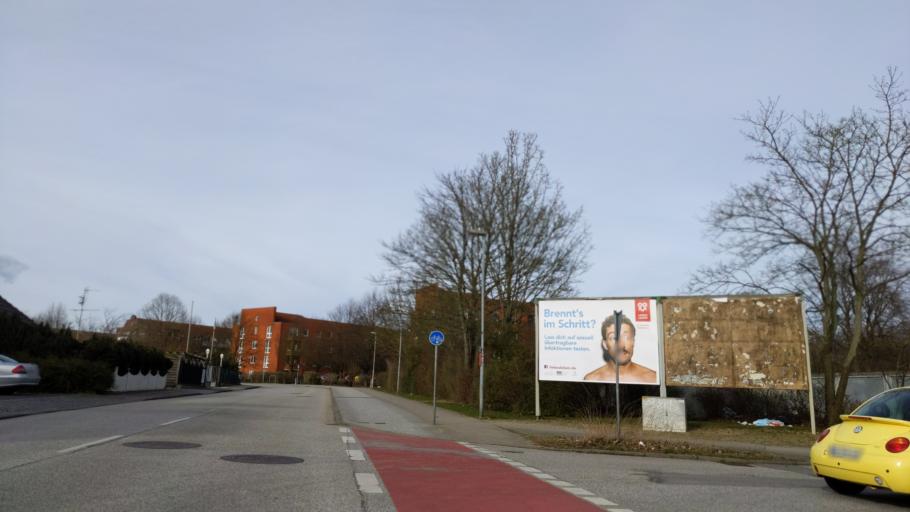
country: DE
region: Mecklenburg-Vorpommern
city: Selmsdorf
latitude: 53.9231
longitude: 10.8220
